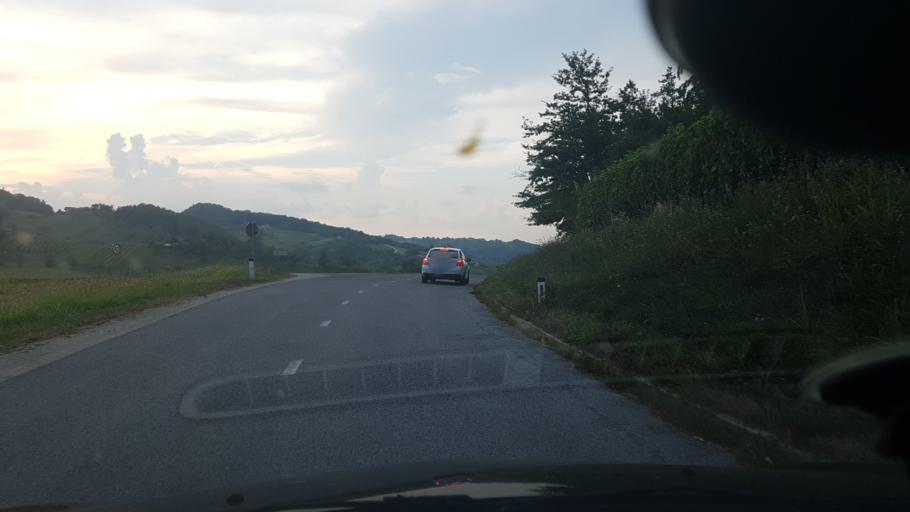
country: SI
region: Kozje
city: Kozje
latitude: 46.0947
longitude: 15.5683
